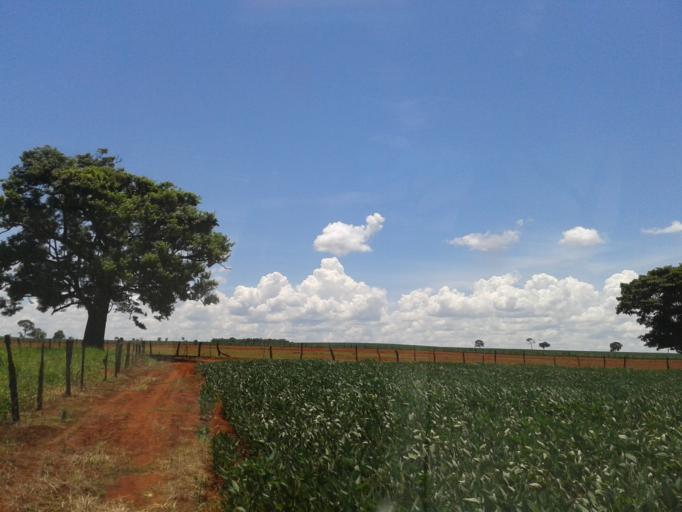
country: BR
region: Minas Gerais
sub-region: Centralina
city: Centralina
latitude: -18.6247
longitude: -49.2783
